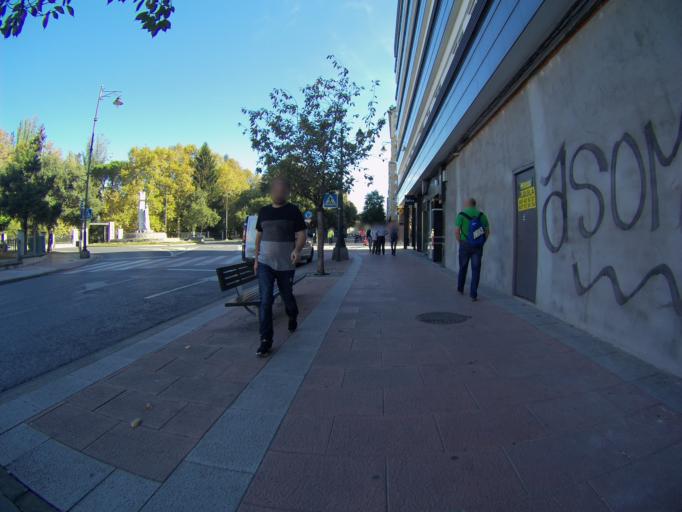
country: ES
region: Castille and Leon
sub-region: Provincia de Leon
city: Ponferrada
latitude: 42.5483
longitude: -6.5858
